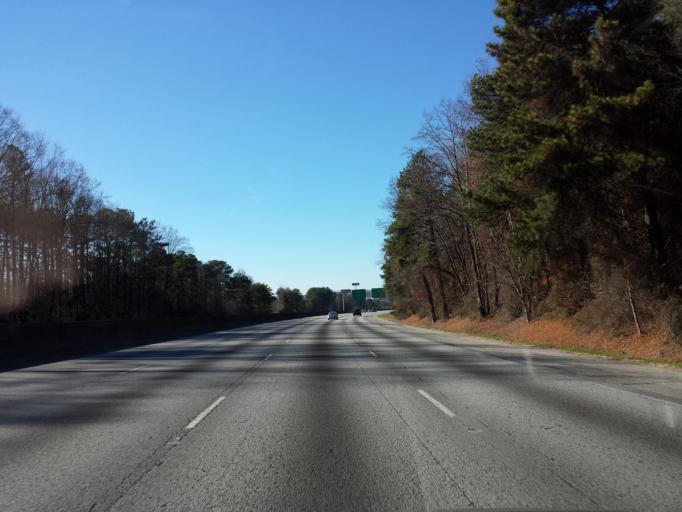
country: US
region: Georgia
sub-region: Cobb County
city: Mableton
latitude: 33.7650
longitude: -84.5188
